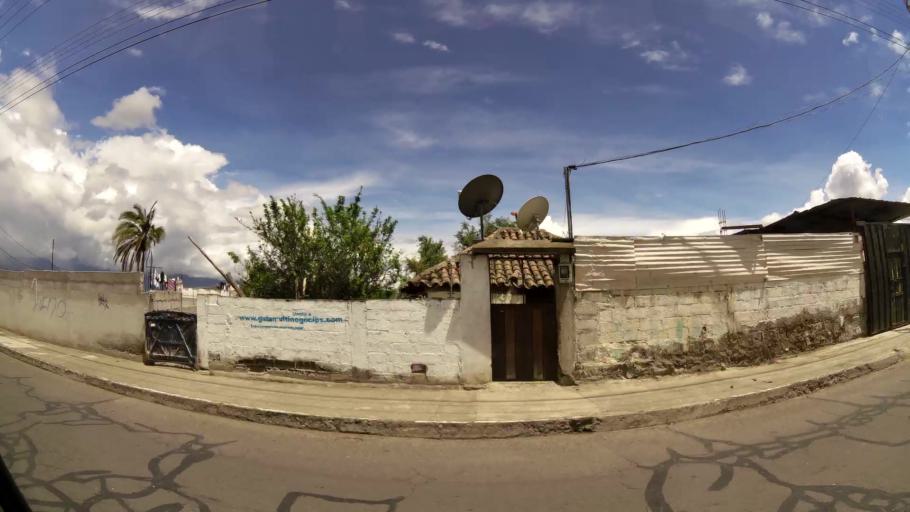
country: EC
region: Tungurahua
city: Ambato
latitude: -1.2773
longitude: -78.6401
